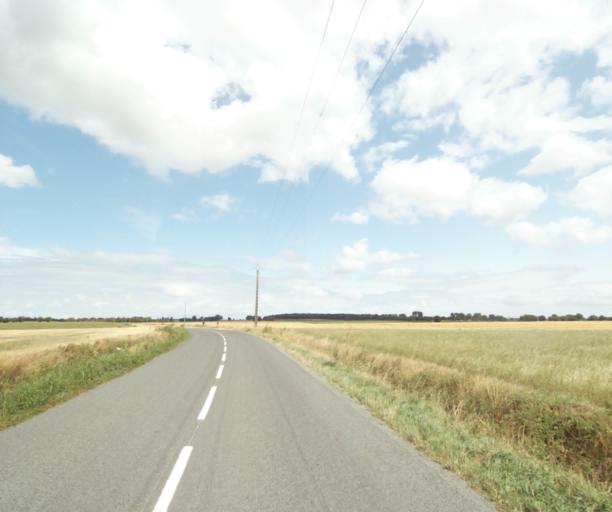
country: FR
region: Pays de la Loire
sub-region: Departement de la Sarthe
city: Sable-sur-Sarthe
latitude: 47.8568
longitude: -0.3315
